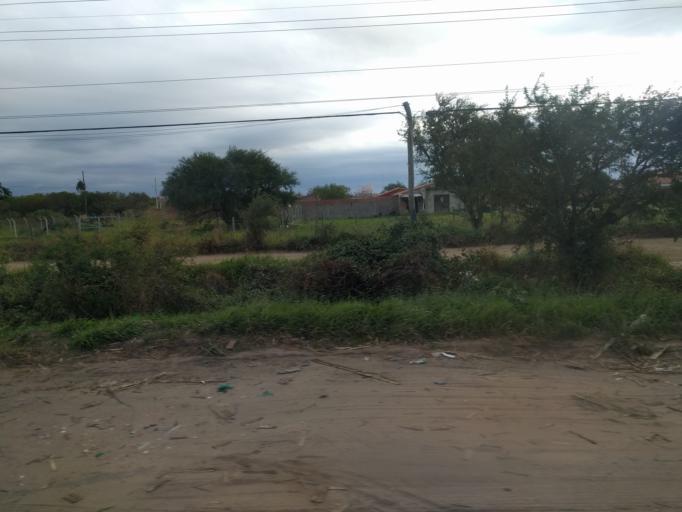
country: BO
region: Santa Cruz
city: La Belgica
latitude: -17.6131
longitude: -63.1595
